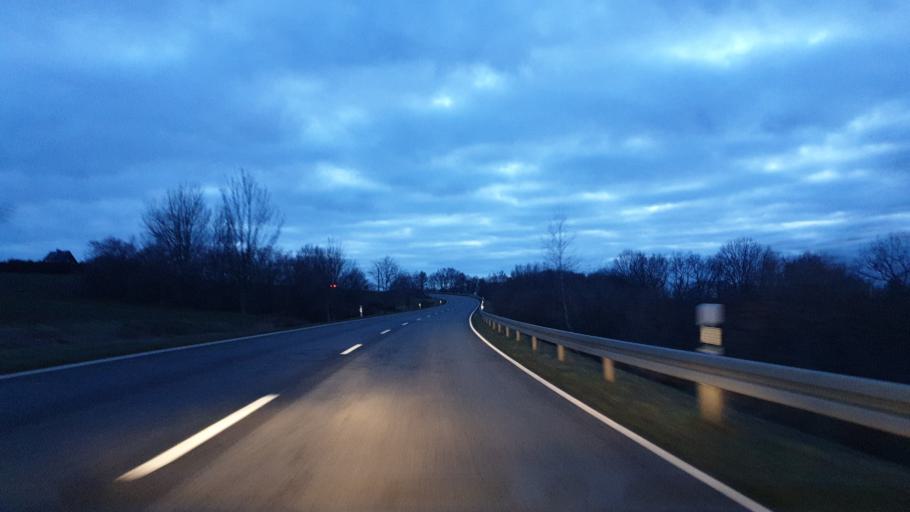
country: DE
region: Saxony
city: Lichtenstein
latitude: 50.7501
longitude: 12.6008
